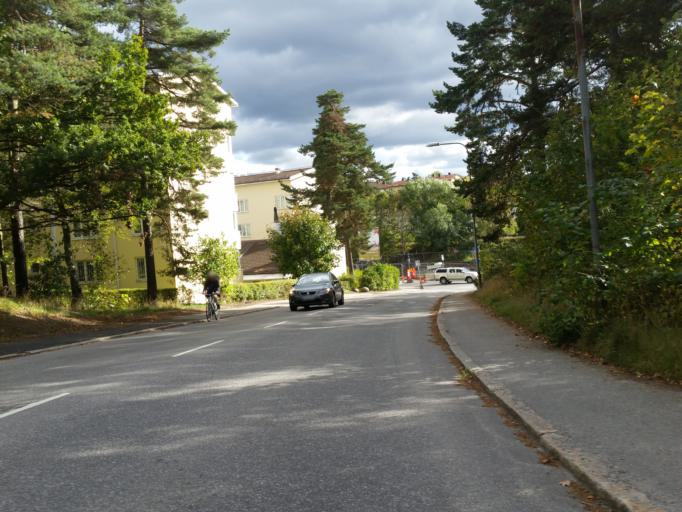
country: SE
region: Stockholm
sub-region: Stockholms Kommun
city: OEstermalm
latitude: 59.2958
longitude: 18.0964
